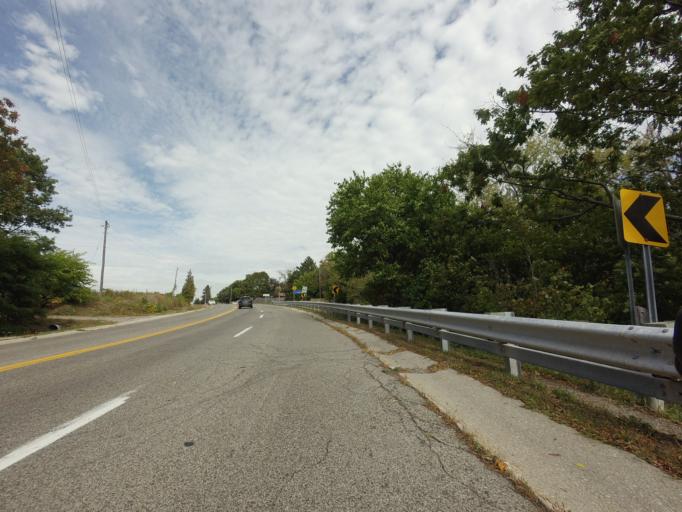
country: CA
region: Ontario
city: Ancaster
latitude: 43.2783
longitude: -79.9494
